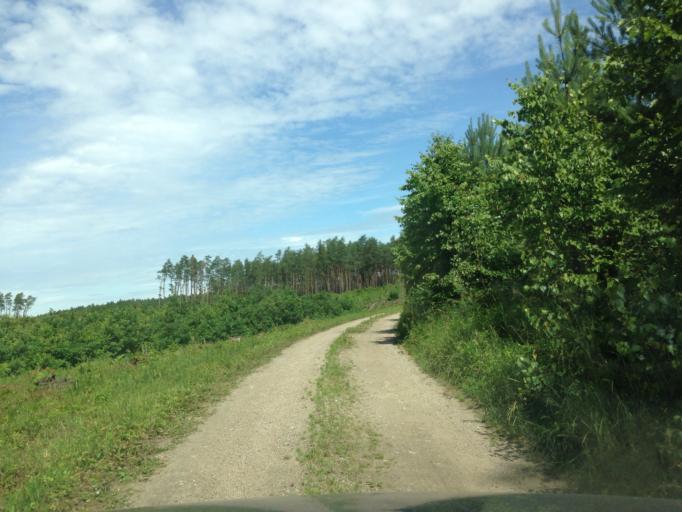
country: PL
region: Kujawsko-Pomorskie
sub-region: Powiat brodnicki
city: Bartniczka
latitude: 53.2725
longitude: 19.5694
